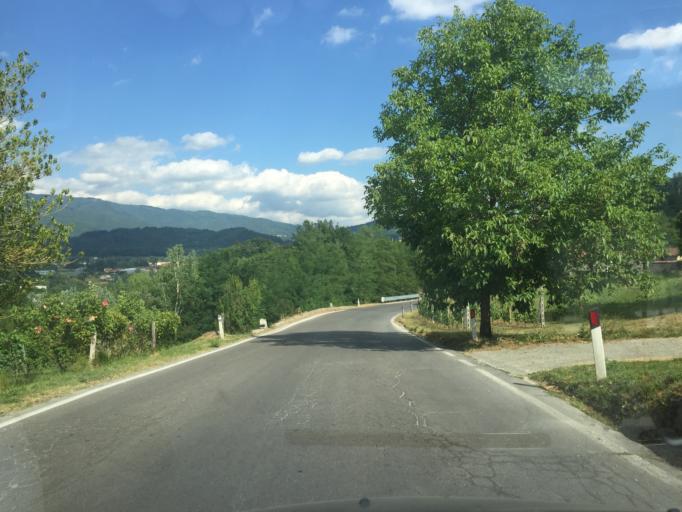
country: IT
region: Tuscany
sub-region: Provincia di Lucca
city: Castelnuovo di Garfagnana
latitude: 44.1269
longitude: 10.3854
